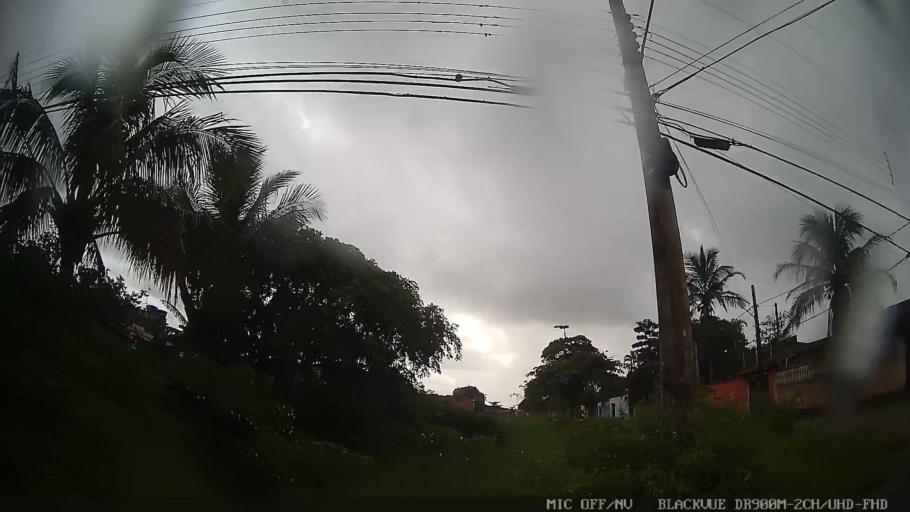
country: BR
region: Sao Paulo
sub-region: Itanhaem
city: Itanhaem
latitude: -24.2303
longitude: -46.8798
